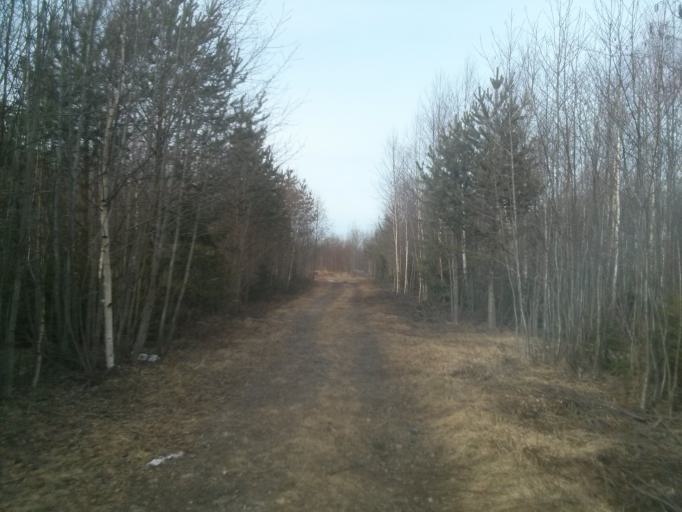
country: SE
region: Vaesternorrland
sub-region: Sundsvalls Kommun
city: Njurundabommen
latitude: 62.2374
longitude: 17.3839
